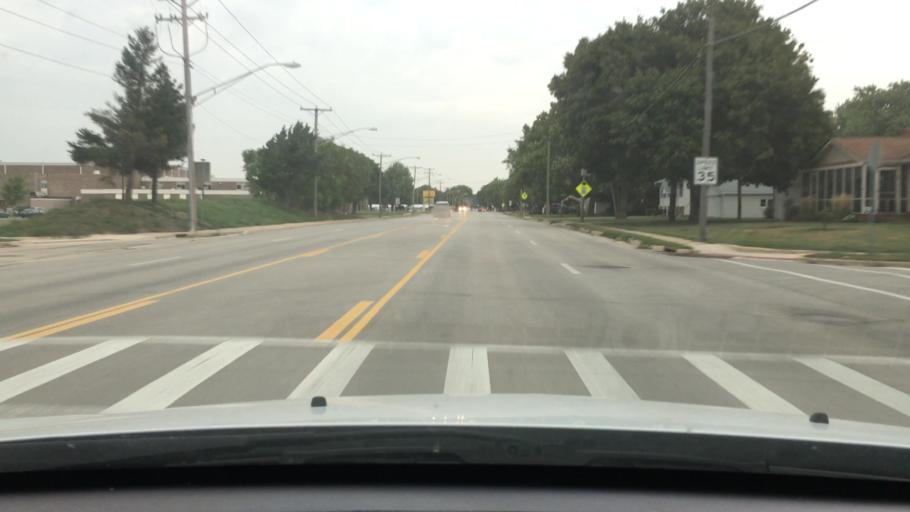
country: US
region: Illinois
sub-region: DeKalb County
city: DeKalb
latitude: 41.9095
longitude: -88.7535
